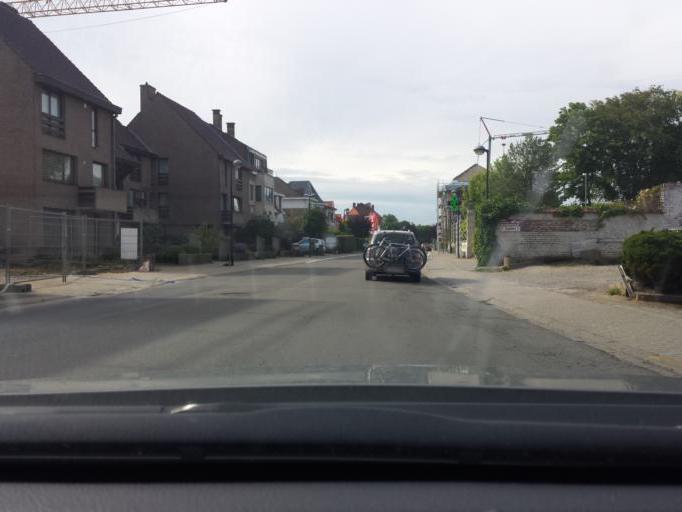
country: BE
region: Flanders
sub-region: Provincie Vlaams-Brabant
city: Kortenberg
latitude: 50.8886
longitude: 4.5439
